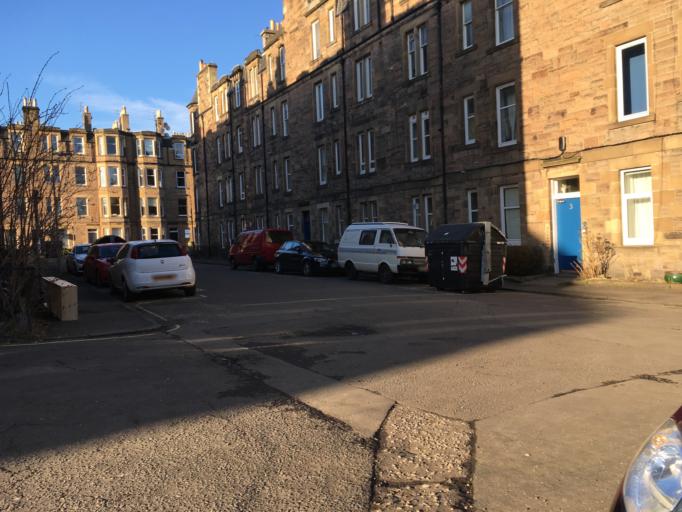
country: GB
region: Scotland
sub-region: Edinburgh
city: Edinburgh
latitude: 55.9267
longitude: -3.2111
